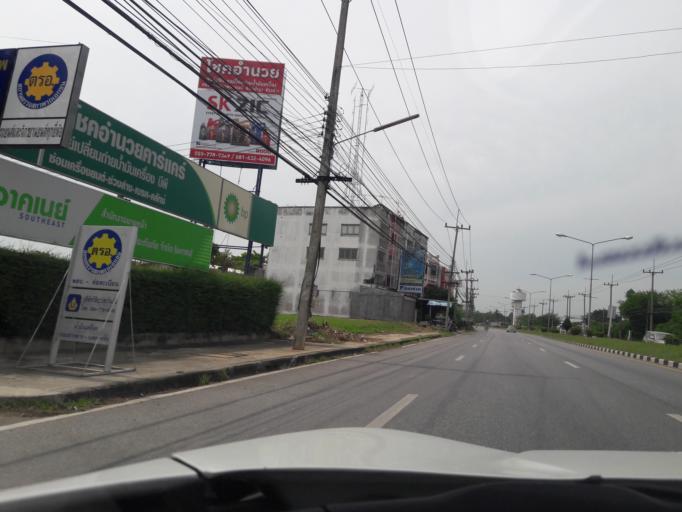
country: TH
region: Lop Buri
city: Ban Mi
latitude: 15.0453
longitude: 100.5536
